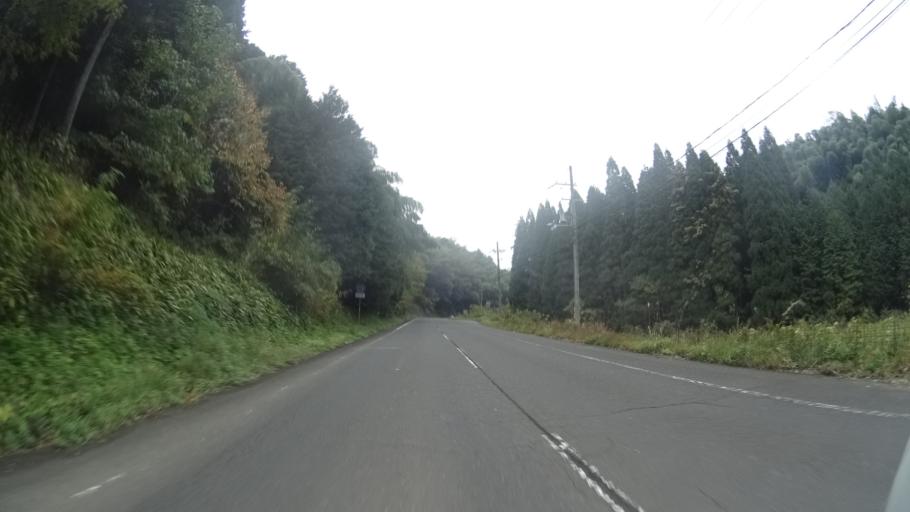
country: JP
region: Kyoto
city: Maizuru
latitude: 35.5092
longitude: 135.4527
